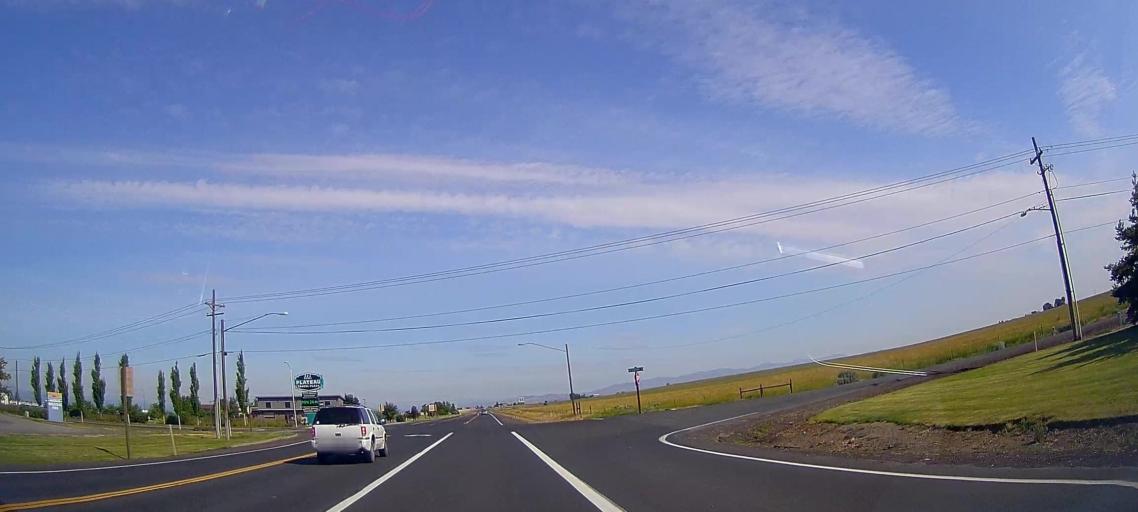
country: US
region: Oregon
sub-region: Jefferson County
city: Madras
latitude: 44.6644
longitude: -121.1356
